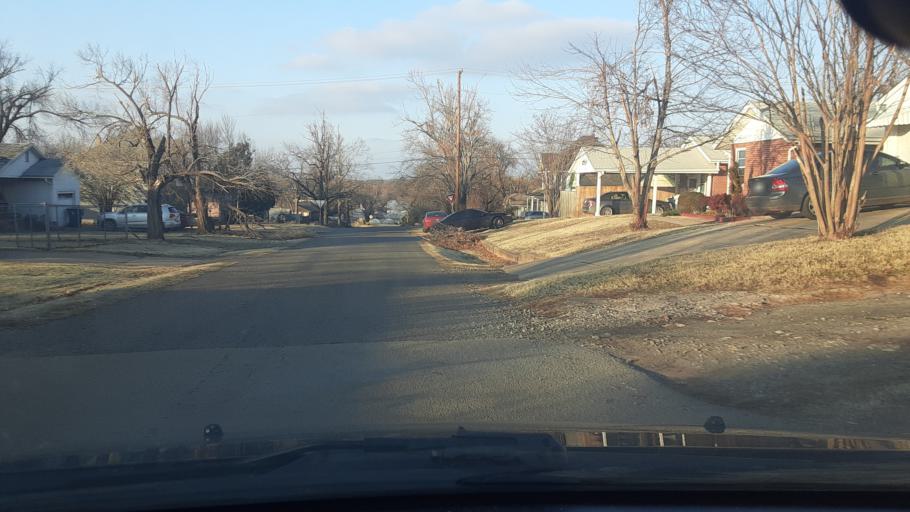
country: US
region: Oklahoma
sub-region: Logan County
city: Guthrie
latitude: 35.8848
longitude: -97.4215
